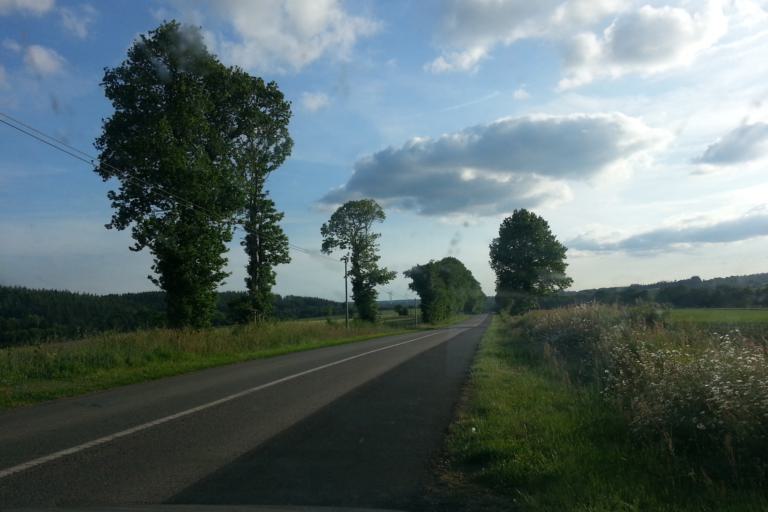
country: FR
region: Brittany
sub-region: Departement du Morbihan
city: Cleguerec
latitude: 48.0947
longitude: -3.0854
